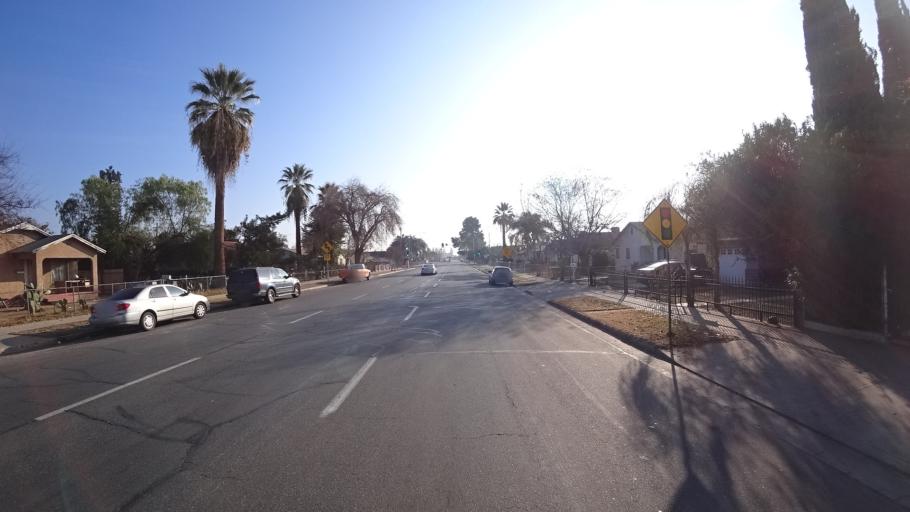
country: US
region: California
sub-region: Kern County
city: Bakersfield
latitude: 35.3786
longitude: -118.9817
